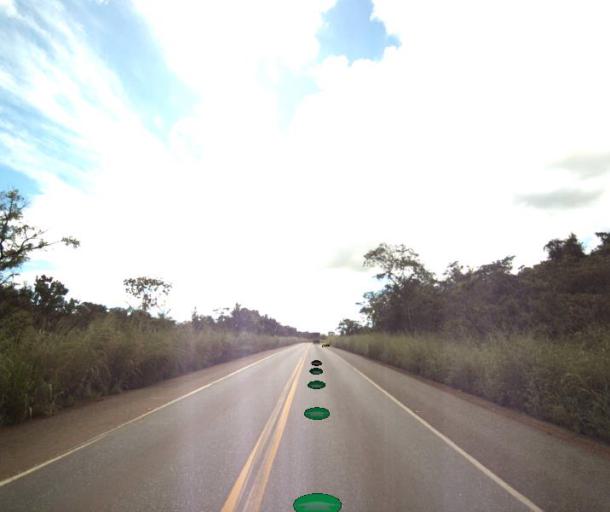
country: BR
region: Goias
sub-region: Jaragua
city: Jaragua
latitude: -15.9015
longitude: -49.2320
